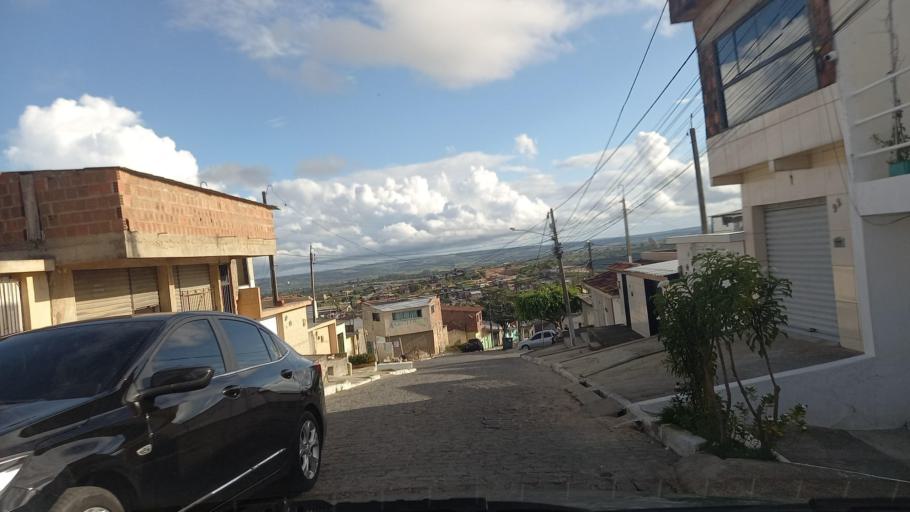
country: BR
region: Pernambuco
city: Garanhuns
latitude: -8.8989
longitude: -36.4981
